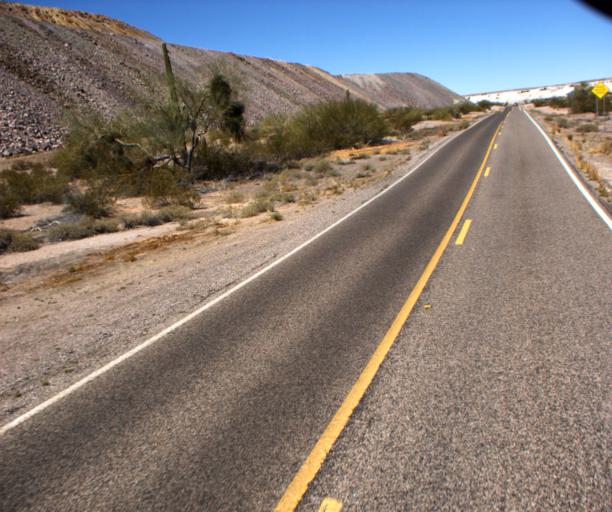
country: US
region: Arizona
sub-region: Pima County
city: Ajo
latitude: 32.3595
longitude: -112.8319
